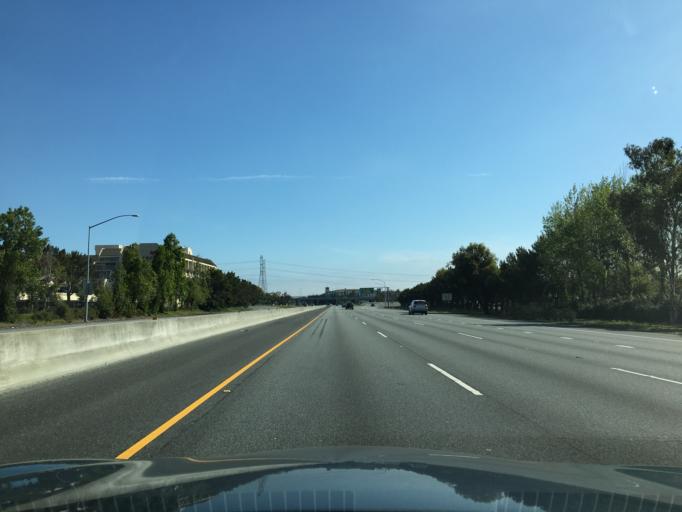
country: US
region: California
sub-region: San Mateo County
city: Foster City
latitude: 37.5604
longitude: -122.2785
